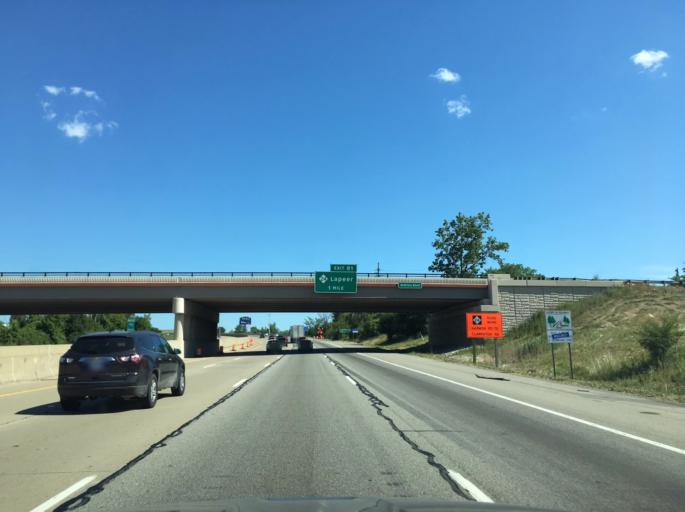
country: US
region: Michigan
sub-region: Oakland County
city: Auburn Hills
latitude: 42.6778
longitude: -83.2411
